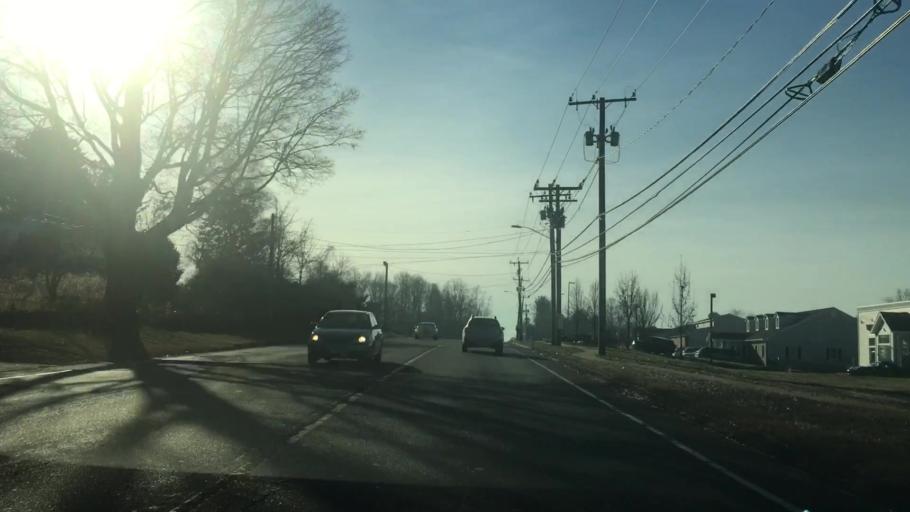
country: US
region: Connecticut
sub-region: Hartford County
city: Plainville
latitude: 41.6348
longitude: -72.9001
